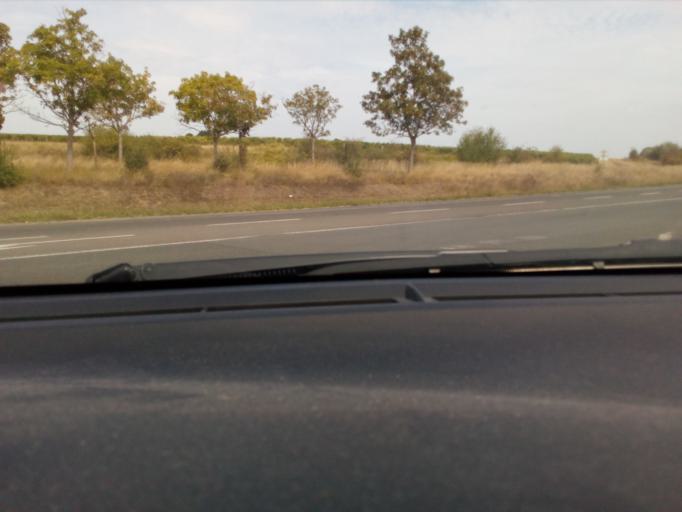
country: FR
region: Poitou-Charentes
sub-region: Departement de la Charente
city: Hiersac
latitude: 45.6711
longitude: 0.0214
